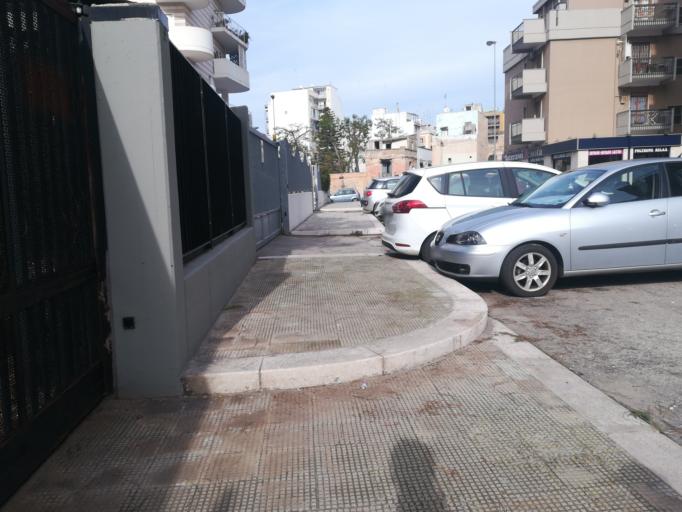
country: IT
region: Apulia
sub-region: Provincia di Bari
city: Bari
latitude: 41.1171
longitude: 16.8834
